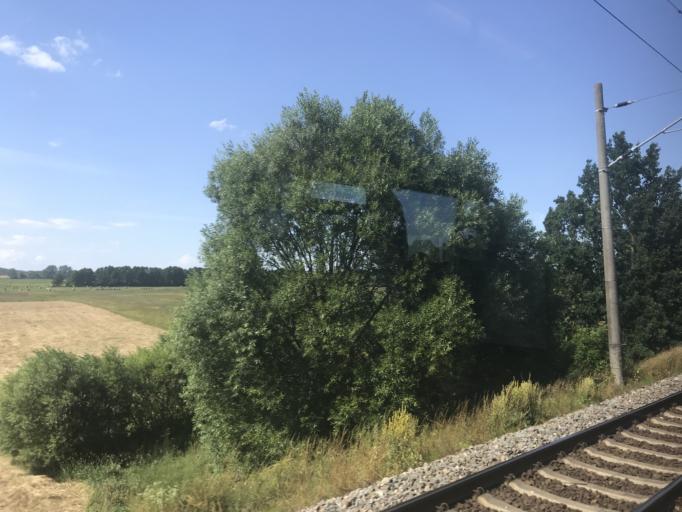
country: DE
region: Brandenburg
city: Pinnow
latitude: 53.0988
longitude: 14.0237
